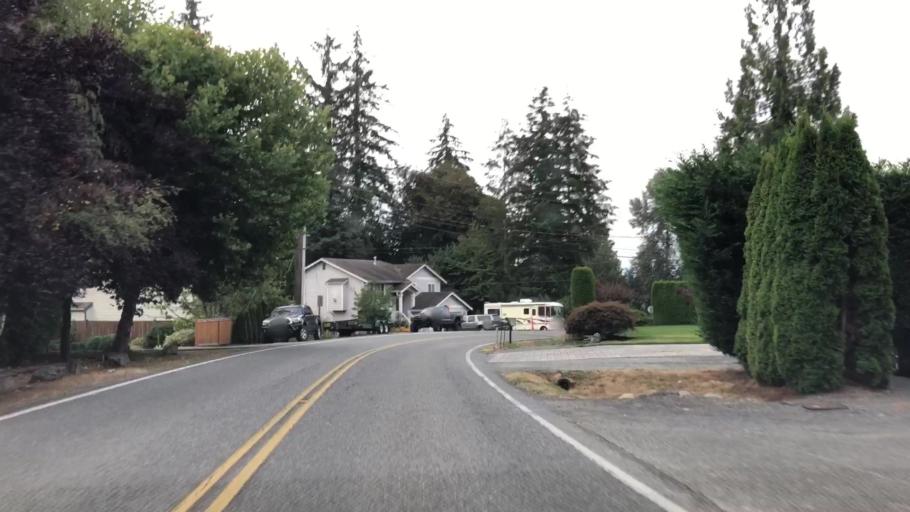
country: US
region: Washington
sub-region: Snohomish County
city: Monroe
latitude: 47.8767
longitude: -121.9881
